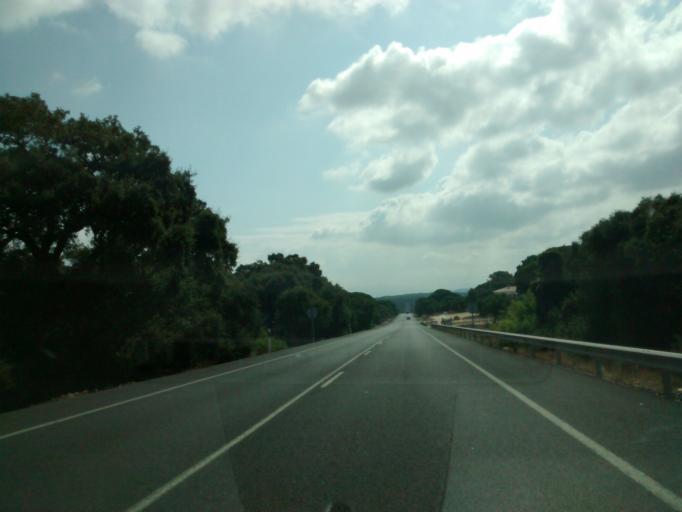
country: ES
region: Andalusia
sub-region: Provincia de Cadiz
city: Vejer de la Frontera
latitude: 36.2539
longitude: -5.9391
